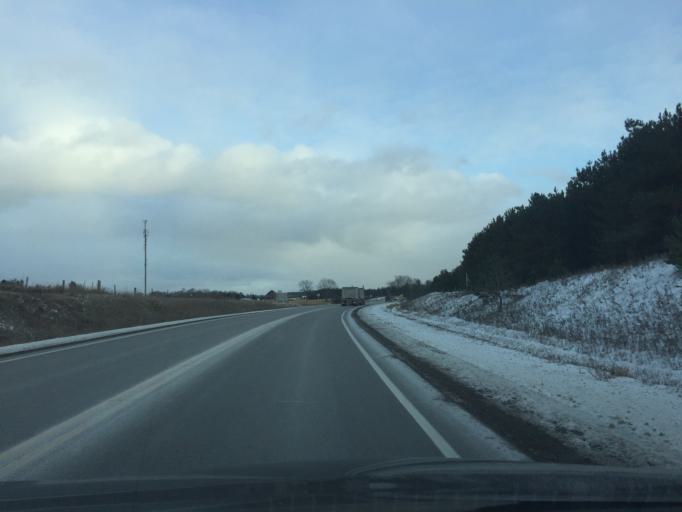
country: CA
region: Ontario
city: Uxbridge
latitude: 44.0607
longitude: -79.0774
